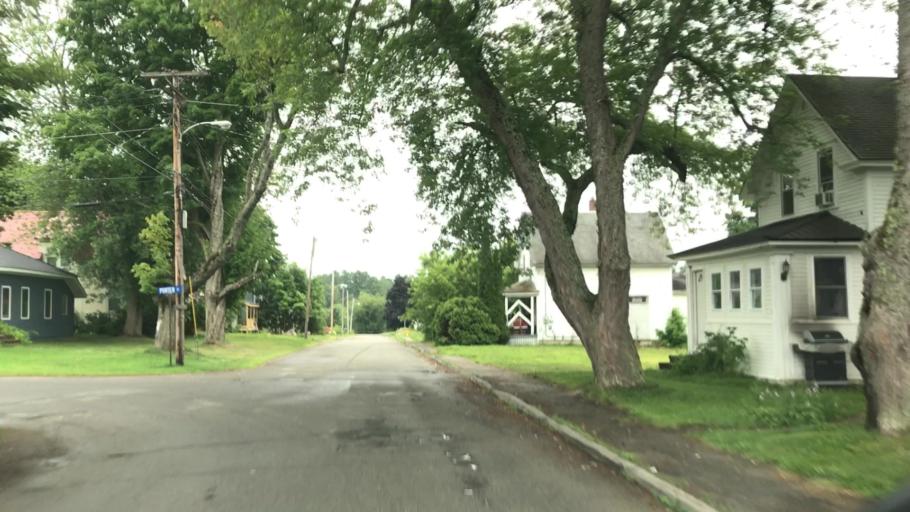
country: US
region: Maine
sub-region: Penobscot County
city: Lincoln
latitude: 45.3666
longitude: -68.4981
